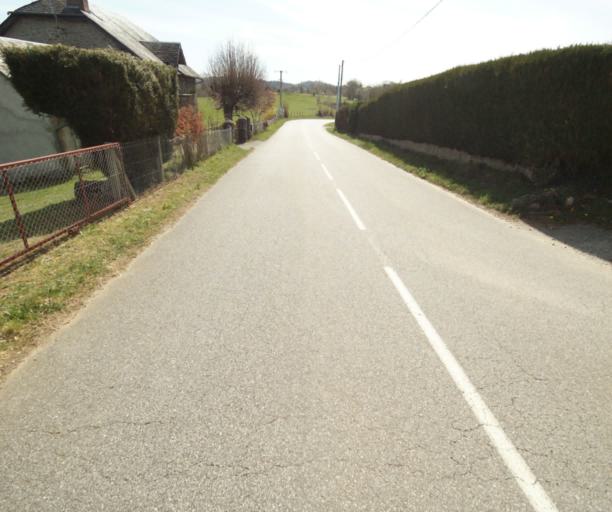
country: FR
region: Limousin
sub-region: Departement de la Correze
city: Naves
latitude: 45.3590
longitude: 1.7970
